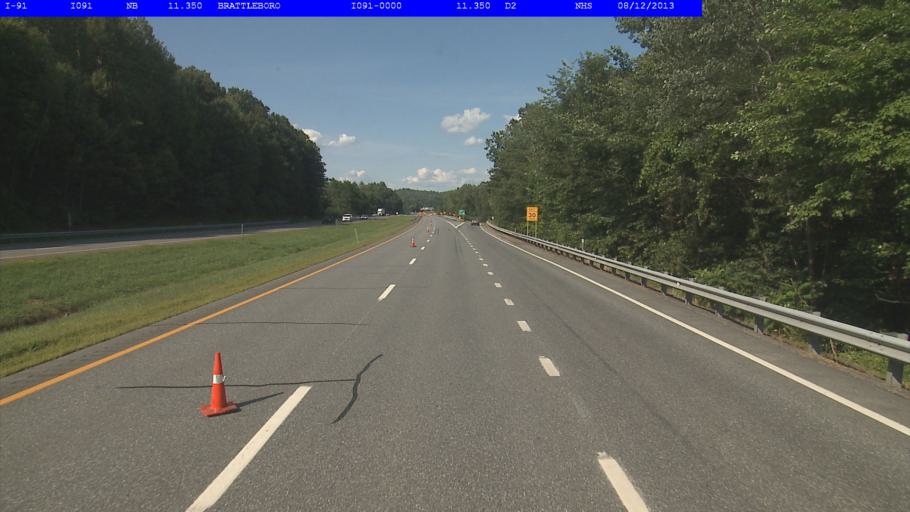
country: US
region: Vermont
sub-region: Windham County
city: Brattleboro
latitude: 42.8834
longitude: -72.5610
